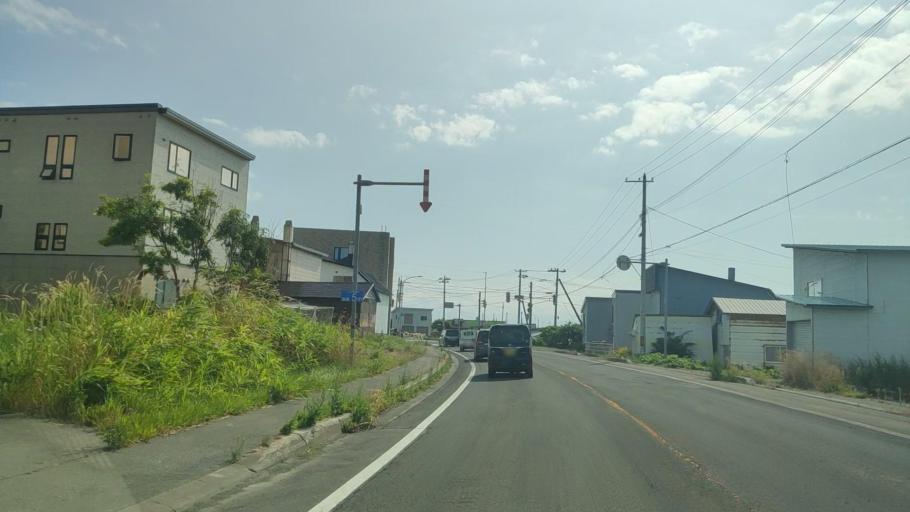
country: JP
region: Hokkaido
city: Rumoi
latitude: 43.9974
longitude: 141.6529
